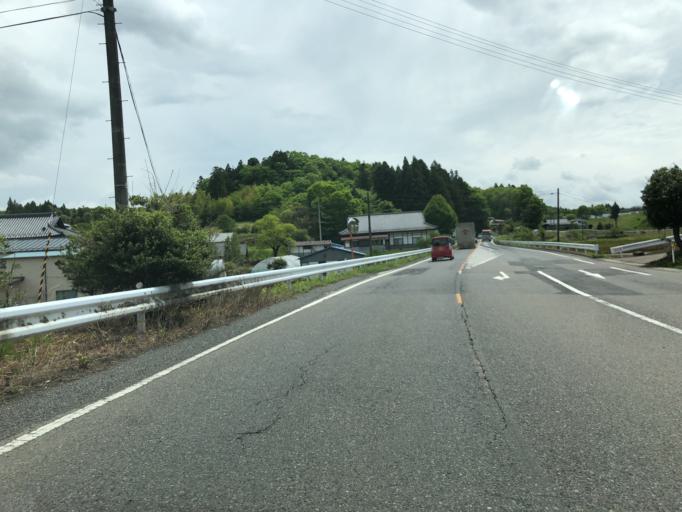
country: JP
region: Fukushima
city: Ishikawa
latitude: 37.0838
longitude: 140.3588
